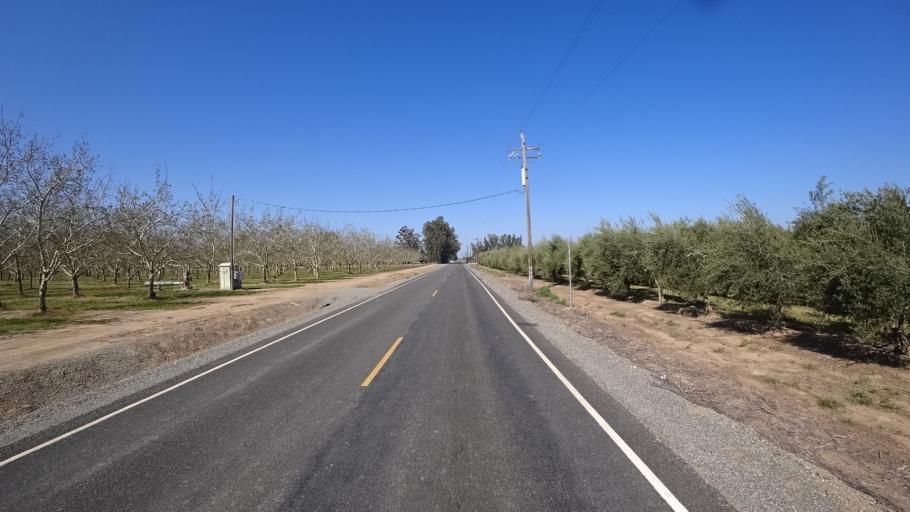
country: US
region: California
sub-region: Glenn County
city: Hamilton City
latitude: 39.6596
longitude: -122.0128
